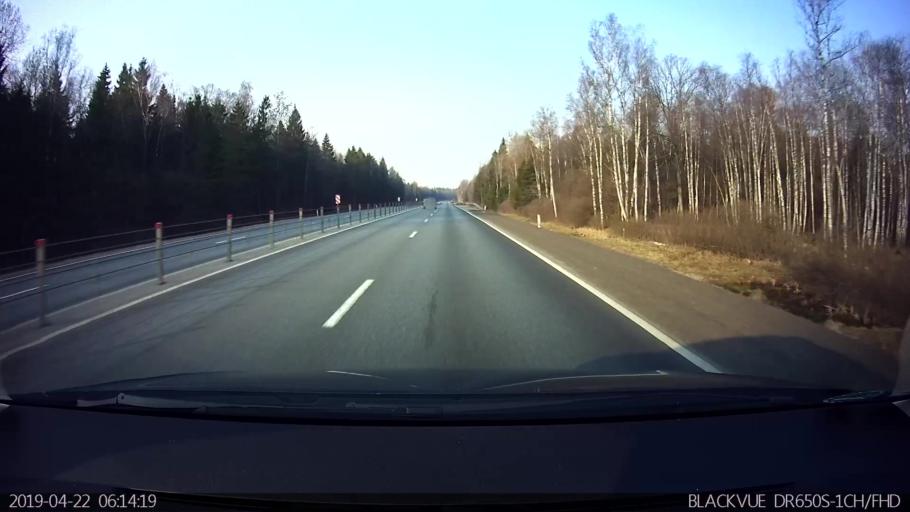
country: RU
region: Moskovskaya
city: Mozhaysk
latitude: 55.4628
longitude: 36.0793
